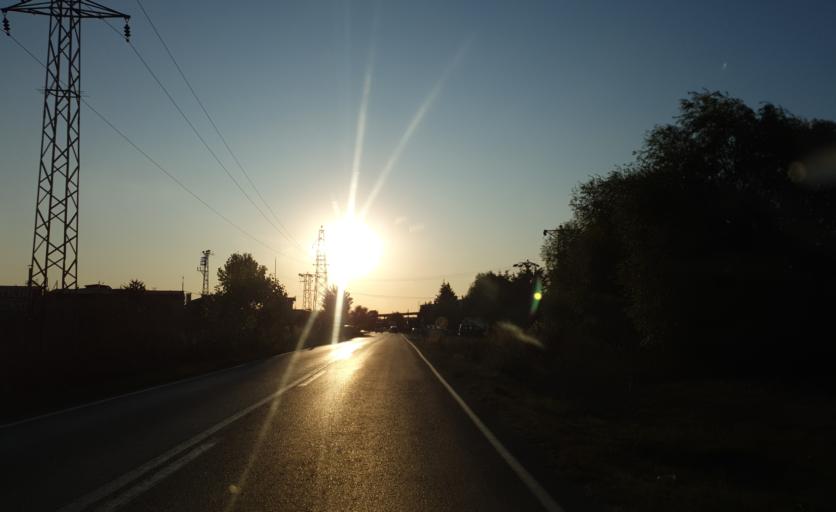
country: TR
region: Tekirdag
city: Beyazkoy
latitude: 41.3368
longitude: 27.7027
